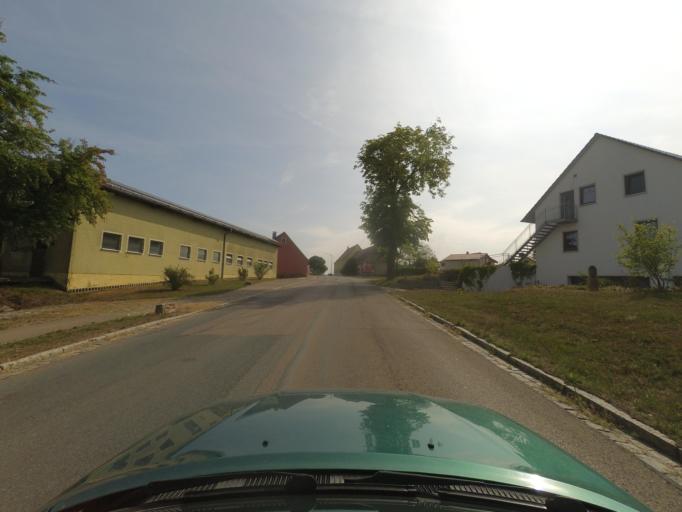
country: DE
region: Bavaria
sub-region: Regierungsbezirk Mittelfranken
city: Feuchtwangen
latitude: 49.1715
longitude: 10.3029
